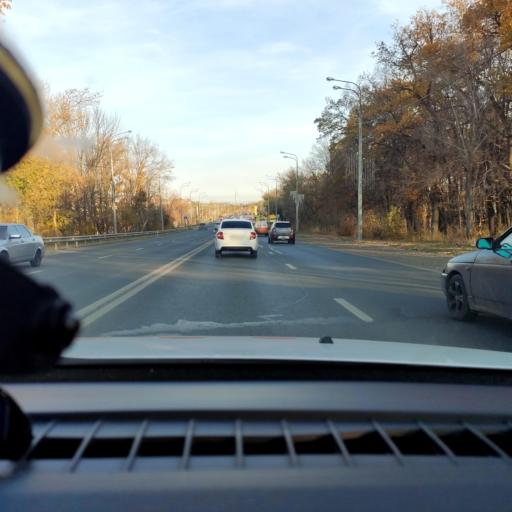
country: RU
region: Samara
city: Samara
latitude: 53.2849
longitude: 50.2270
